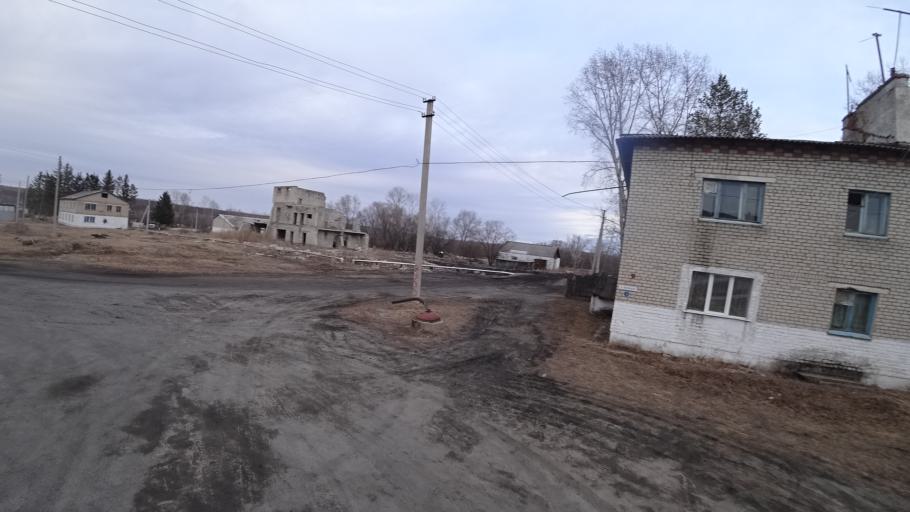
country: RU
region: Amur
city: Bureya
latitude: 50.0182
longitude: 129.7704
